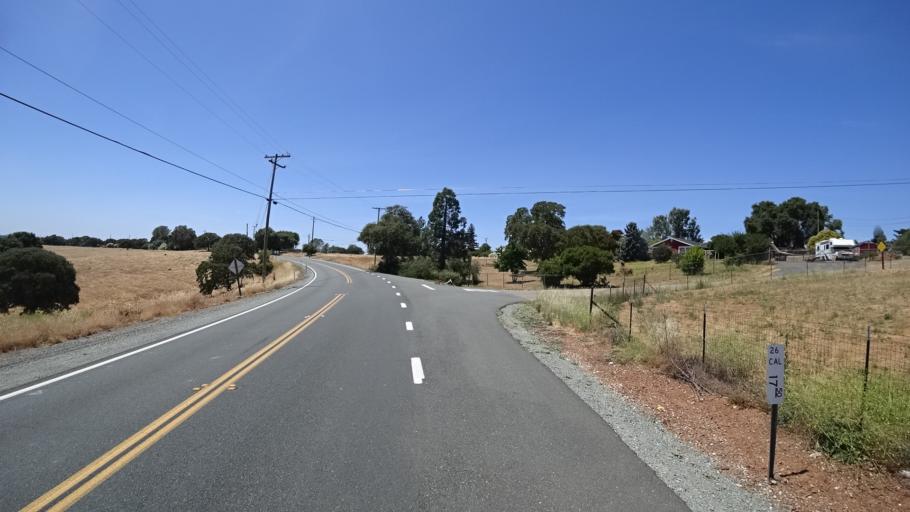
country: US
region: California
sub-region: Amador County
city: Jackson
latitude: 38.2930
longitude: -120.7089
